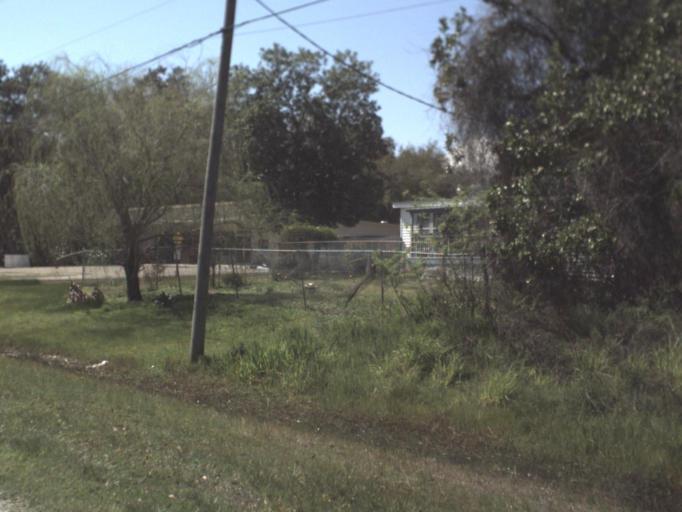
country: US
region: Florida
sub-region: Franklin County
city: Carrabelle
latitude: 29.8803
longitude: -84.5972
